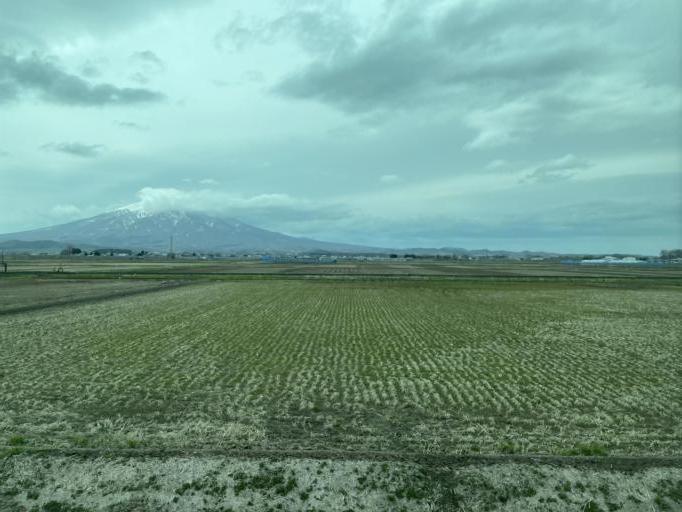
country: JP
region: Aomori
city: Goshogawara
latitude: 40.7314
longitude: 140.4392
